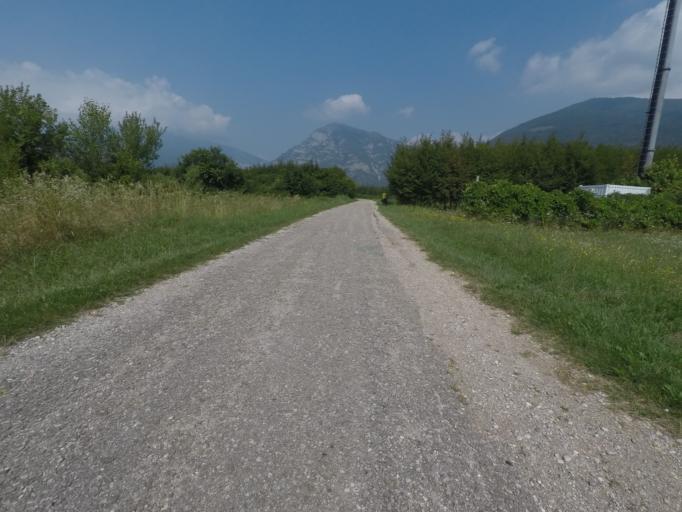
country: IT
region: Friuli Venezia Giulia
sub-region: Provincia di Pordenone
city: Vajont
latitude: 46.1556
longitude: 12.6937
